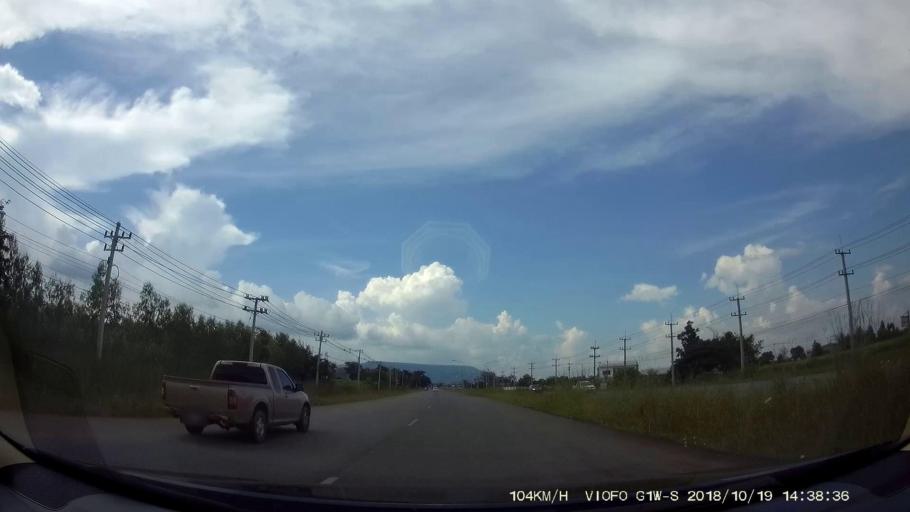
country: TH
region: Chaiyaphum
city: Kaeng Khro
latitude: 16.2153
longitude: 102.2007
